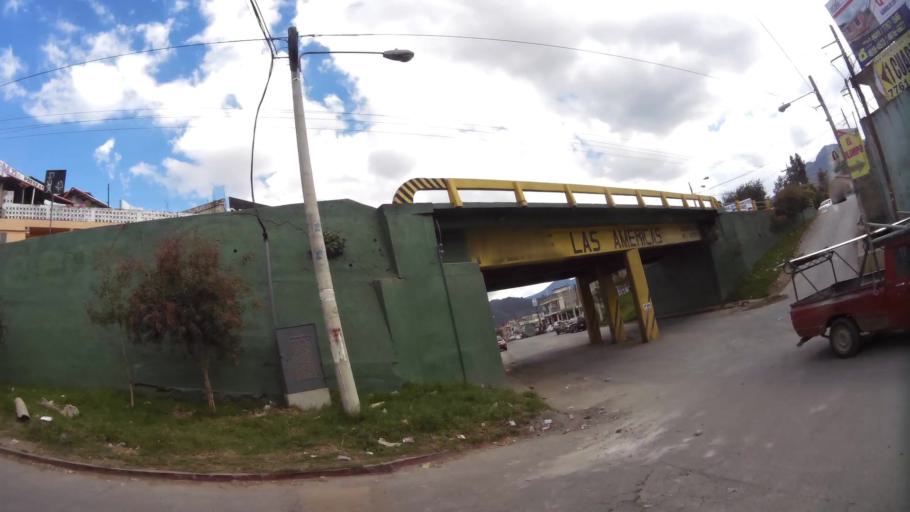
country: GT
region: Quetzaltenango
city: Quetzaltenango
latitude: 14.8401
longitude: -91.5358
